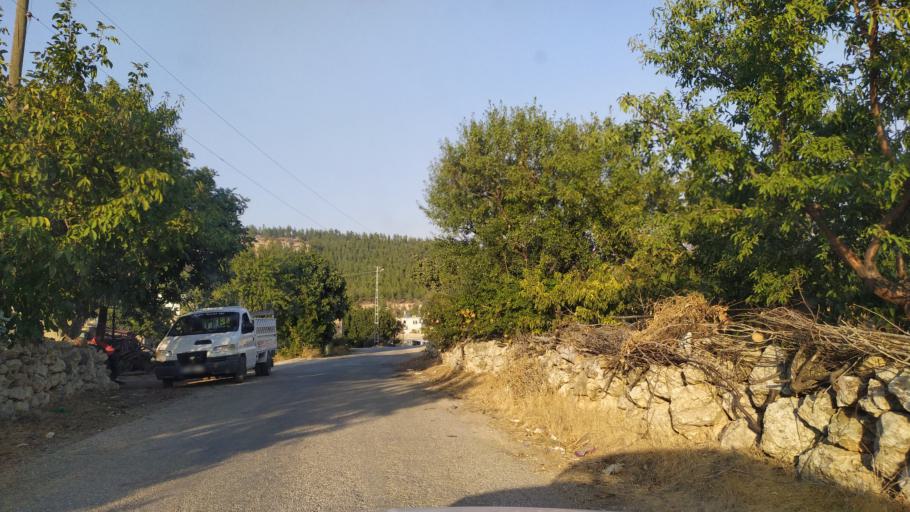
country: TR
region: Mersin
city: Mut
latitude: 36.6923
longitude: 33.1994
